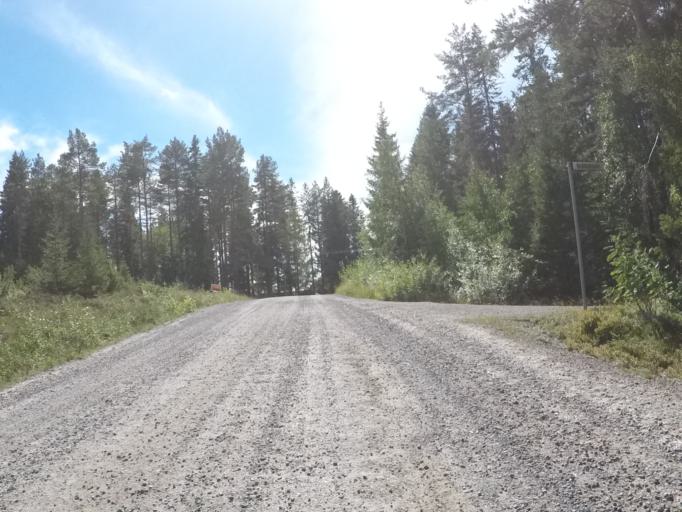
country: SE
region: Vaesterbotten
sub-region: Robertsfors Kommun
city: Robertsfors
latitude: 64.0029
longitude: 20.8118
